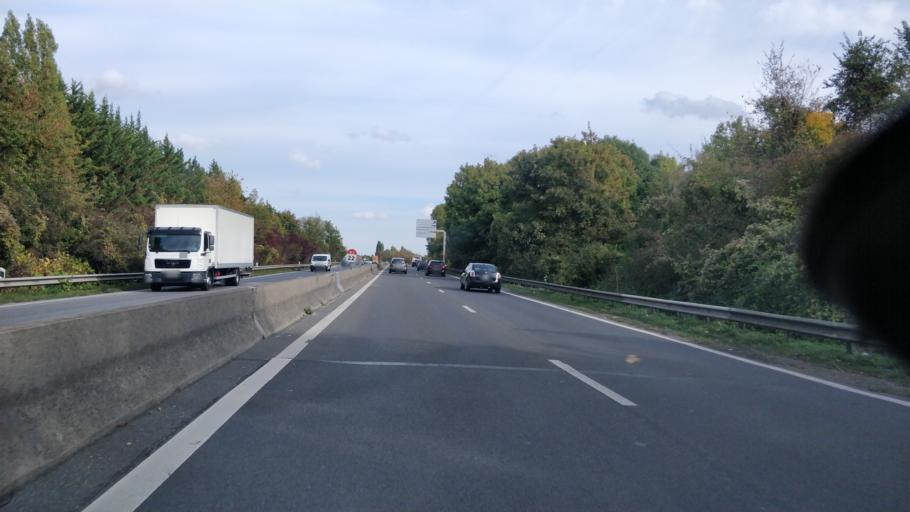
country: FR
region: Ile-de-France
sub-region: Departement de Seine-et-Marne
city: Courtry
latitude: 48.9338
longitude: 2.5962
